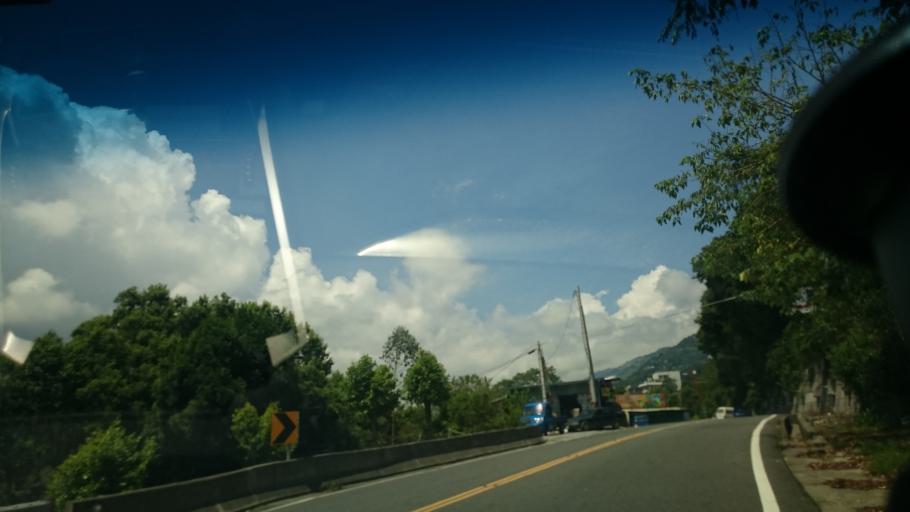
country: TW
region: Taiwan
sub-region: Nantou
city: Puli
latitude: 24.0176
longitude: 121.1292
